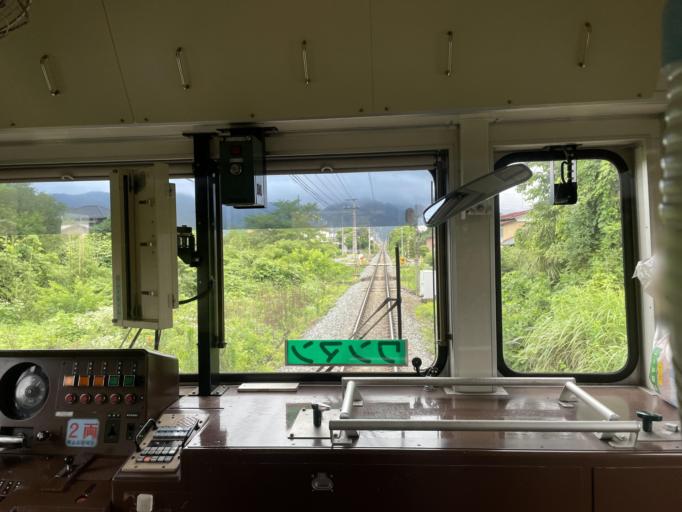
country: JP
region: Saitama
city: Kodamacho-kodamaminami
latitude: 36.1032
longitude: 139.1104
